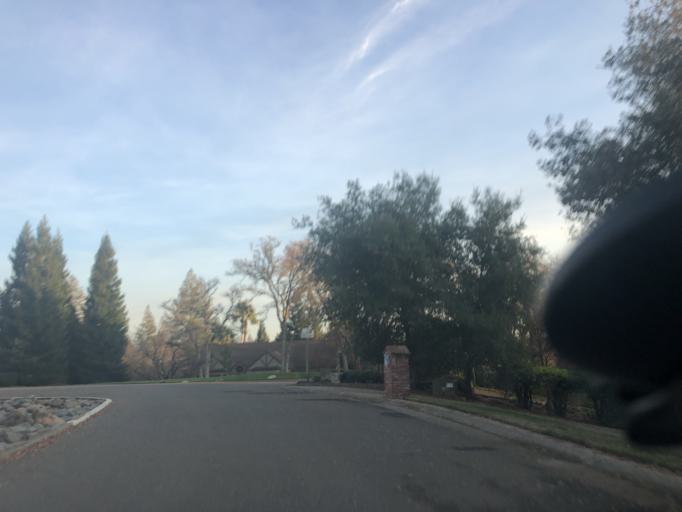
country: US
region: California
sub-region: Sacramento County
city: Gold River
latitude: 38.6407
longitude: -121.2323
